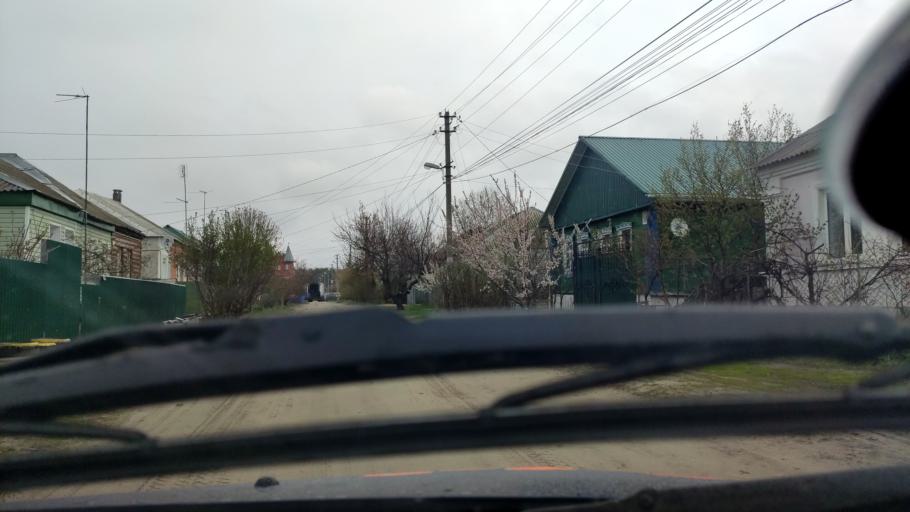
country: RU
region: Voronezj
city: Somovo
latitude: 51.7408
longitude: 39.2627
